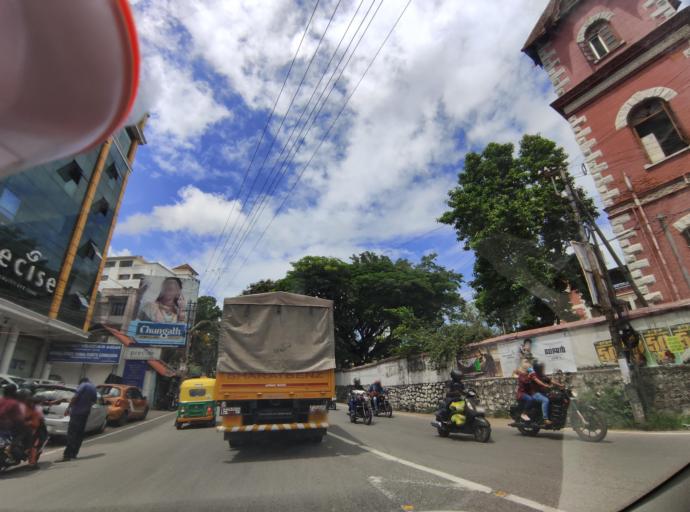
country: IN
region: Kerala
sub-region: Thiruvananthapuram
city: Thiruvananthapuram
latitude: 8.5101
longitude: 76.9486
